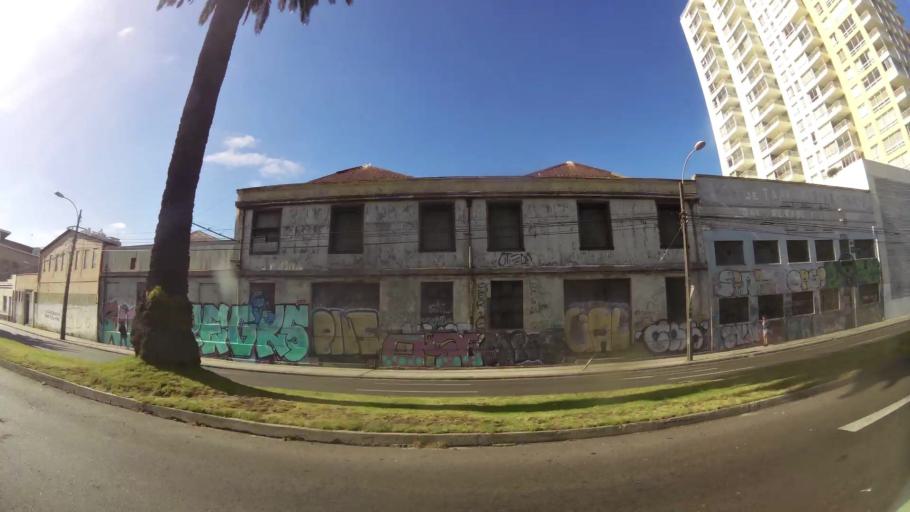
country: CL
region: Valparaiso
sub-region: Provincia de Valparaiso
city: Valparaiso
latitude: -33.0436
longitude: -71.6152
